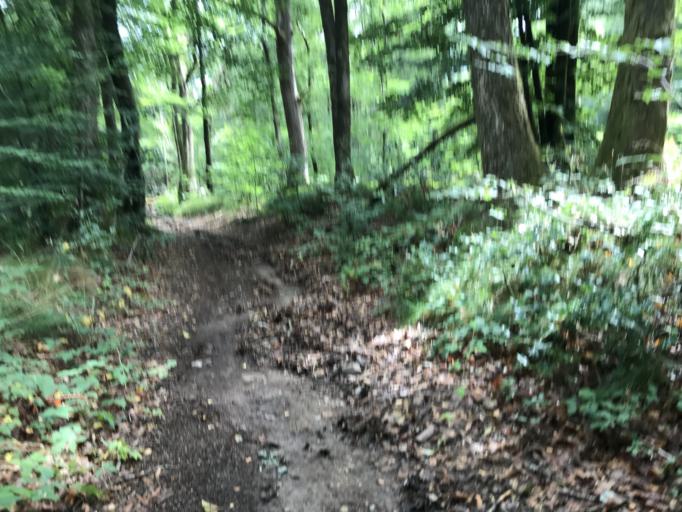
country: FR
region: Champagne-Ardenne
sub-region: Departement des Ardennes
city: Thilay
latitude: 49.8926
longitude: 4.7737
